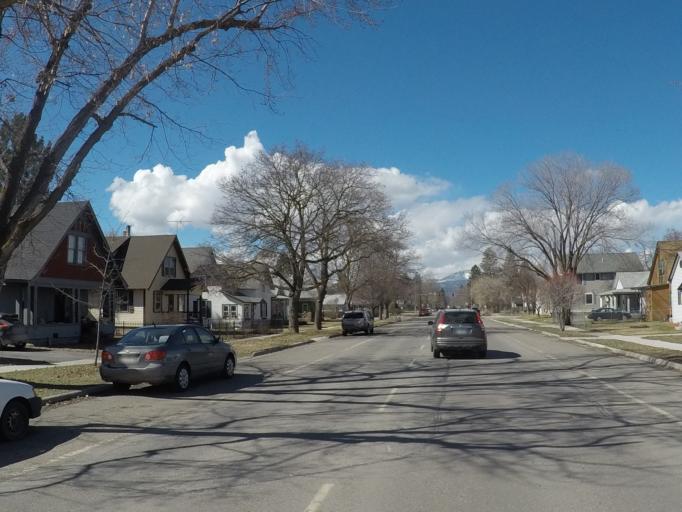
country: US
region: Montana
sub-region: Missoula County
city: Missoula
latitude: 46.8650
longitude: -114.0158
